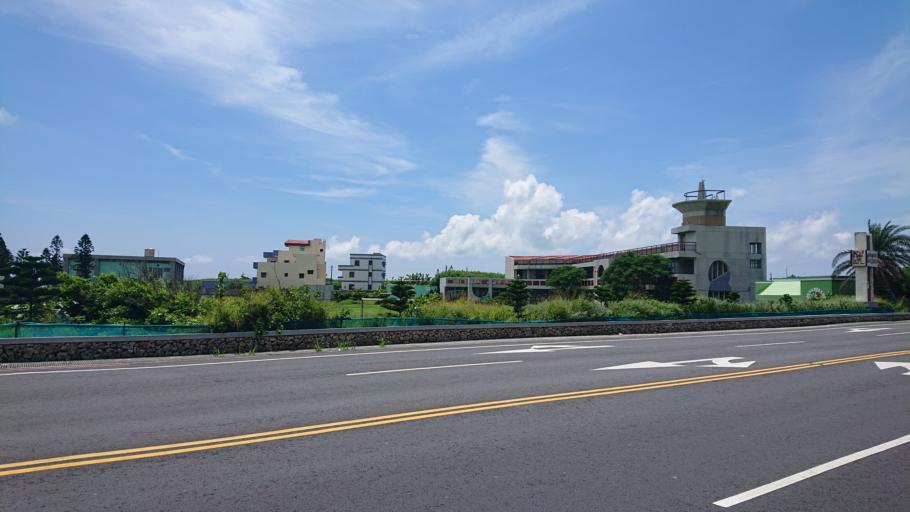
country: TW
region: Taiwan
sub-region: Penghu
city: Ma-kung
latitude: 23.6108
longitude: 119.6096
